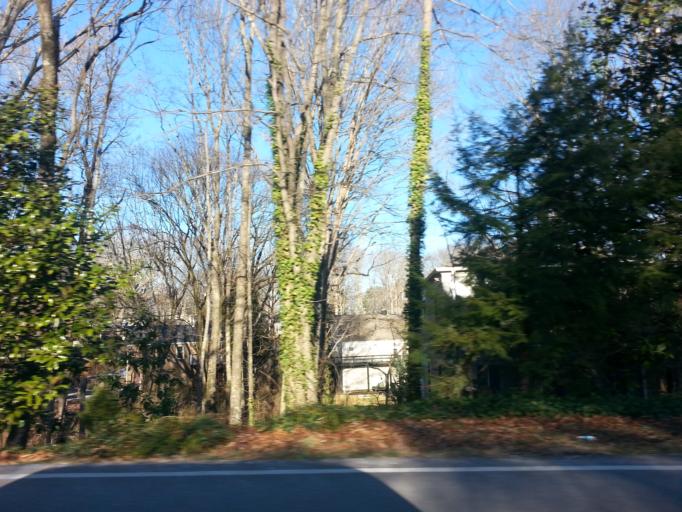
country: US
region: Tennessee
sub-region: Knox County
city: Farragut
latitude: 35.9482
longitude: -84.0577
